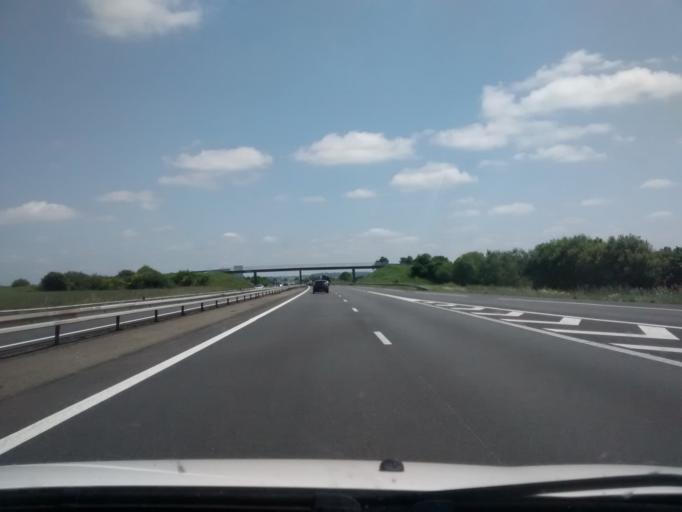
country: FR
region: Pays de la Loire
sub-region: Departement de la Mayenne
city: Sainte-Suzanne
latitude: 48.0263
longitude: -0.3390
